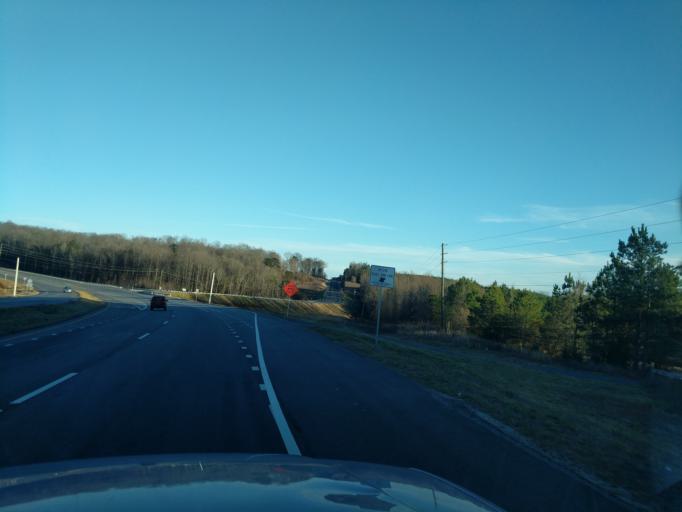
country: US
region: Georgia
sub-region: Stephens County
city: Toccoa
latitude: 34.5208
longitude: -83.2406
